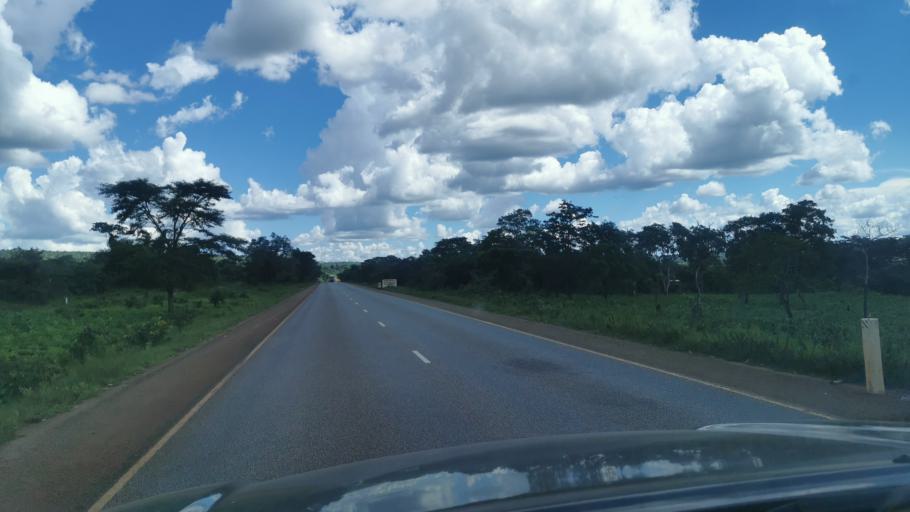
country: TZ
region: Geita
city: Uyovu
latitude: -3.0955
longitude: 31.3004
